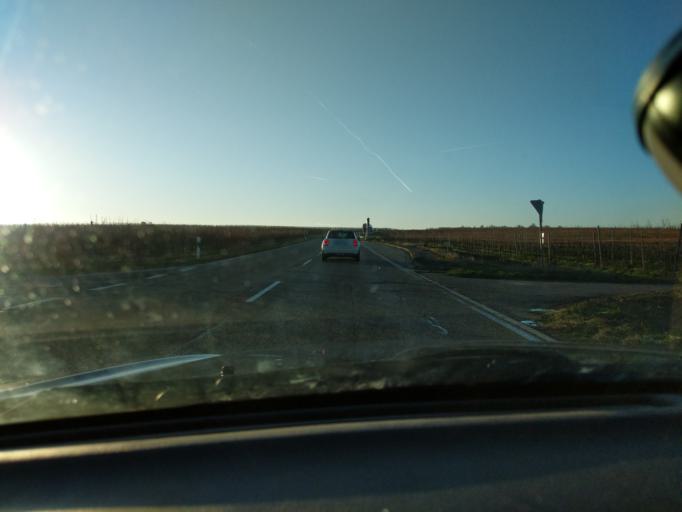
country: DE
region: Rheinland-Pfalz
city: Dackenheim
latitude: 49.5198
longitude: 8.1789
